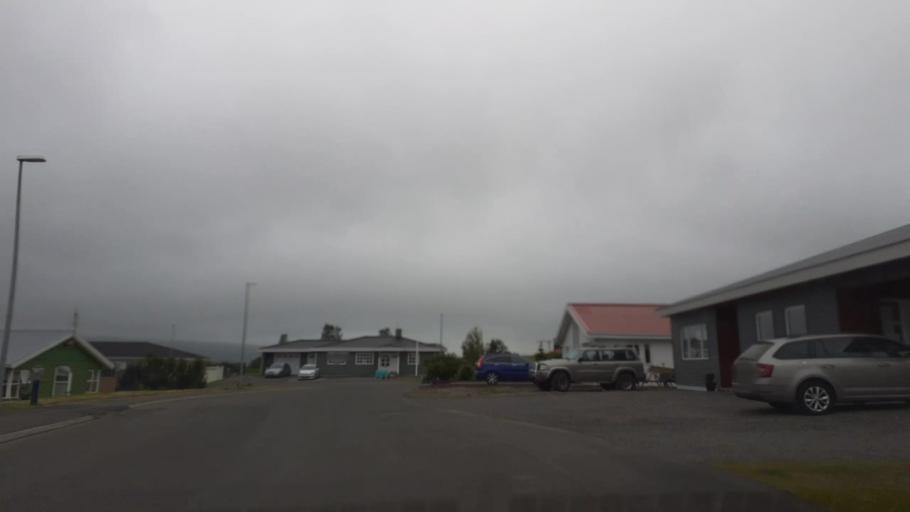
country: IS
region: Northeast
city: Dalvik
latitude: 65.9688
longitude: -18.5448
